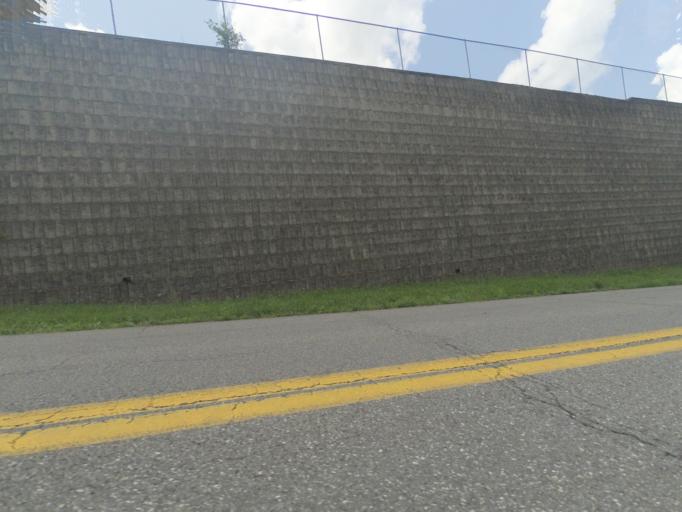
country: US
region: West Virginia
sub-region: Cabell County
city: Pea Ridge
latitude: 38.4066
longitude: -82.3738
